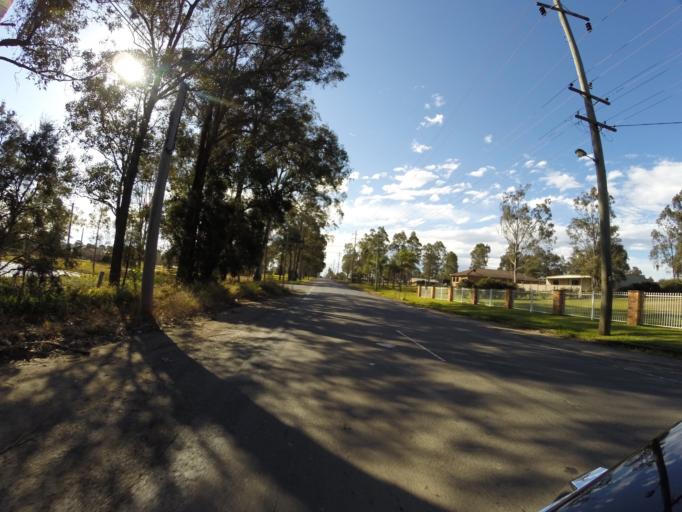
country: AU
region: New South Wales
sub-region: Fairfield
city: Cecil Park
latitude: -33.8979
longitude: 150.7894
